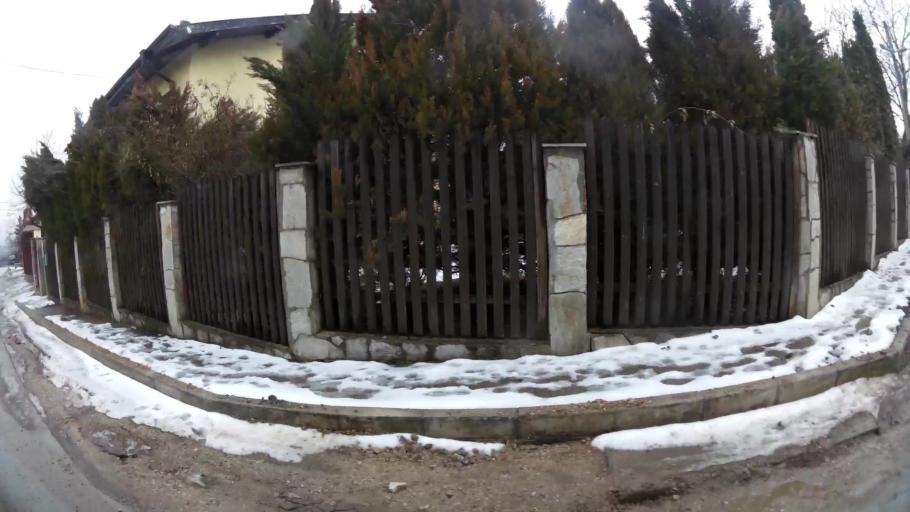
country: BG
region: Sofiya
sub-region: Obshtina Bozhurishte
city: Bozhurishte
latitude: 42.6832
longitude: 23.2338
